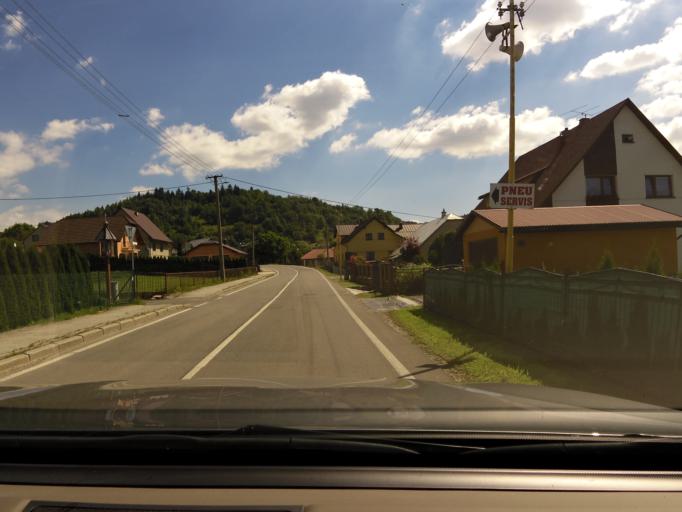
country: PL
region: Silesian Voivodeship
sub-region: Powiat cieszynski
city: Koniakow
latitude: 49.5013
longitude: 18.9489
